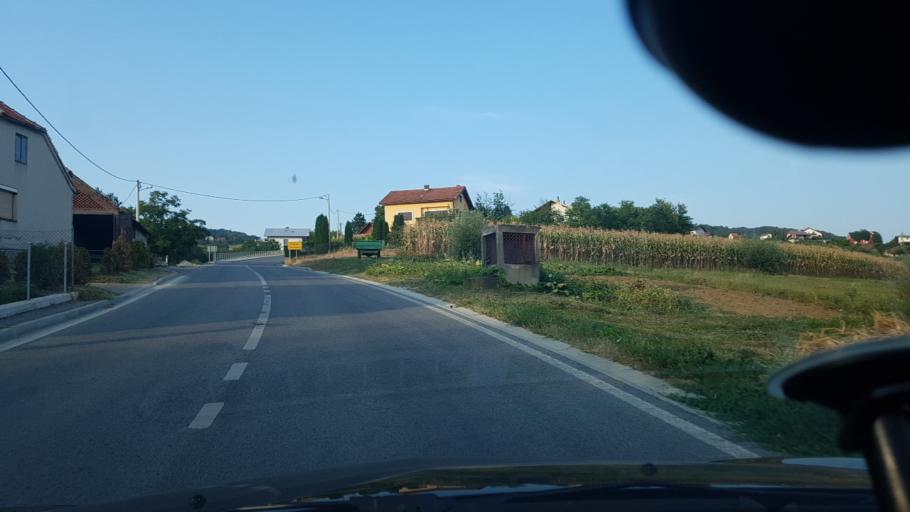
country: HR
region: Krapinsko-Zagorska
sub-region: Grad Krapina
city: Krapina
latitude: 46.1660
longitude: 15.8210
